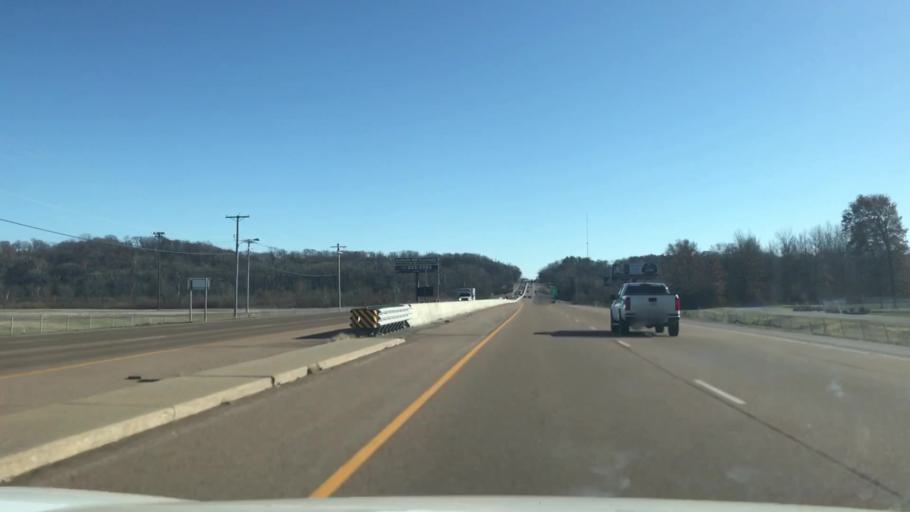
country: US
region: Illinois
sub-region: Saint Clair County
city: Alorton
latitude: 38.5732
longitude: -90.0977
